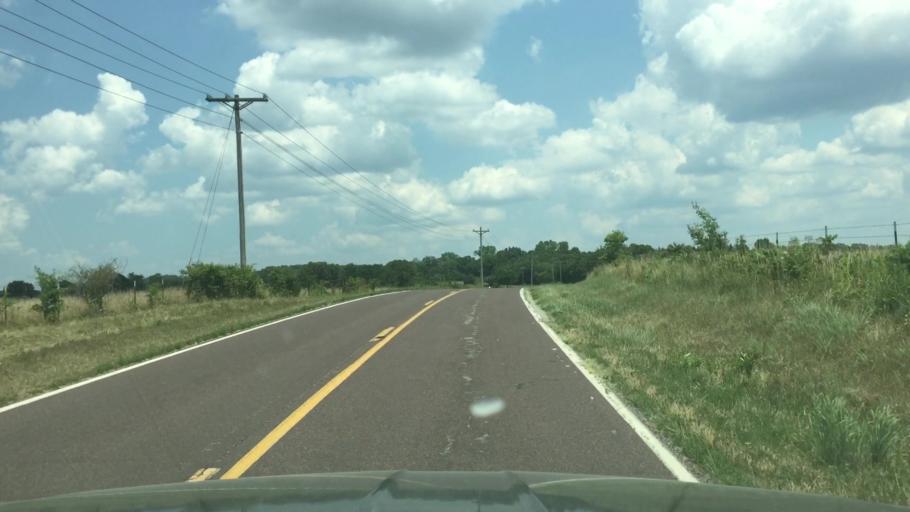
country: US
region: Missouri
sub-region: Miller County
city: Tuscumbia
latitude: 38.1011
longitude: -92.4767
